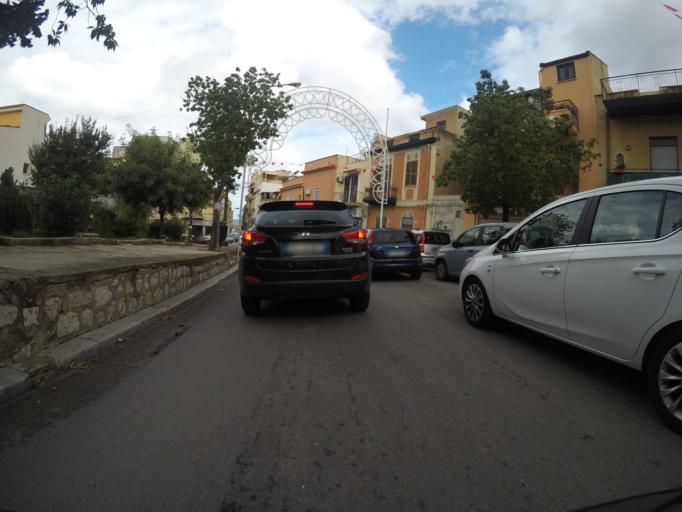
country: IT
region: Sicily
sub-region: Palermo
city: Isola delle Femmine
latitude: 38.1983
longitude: 13.2769
